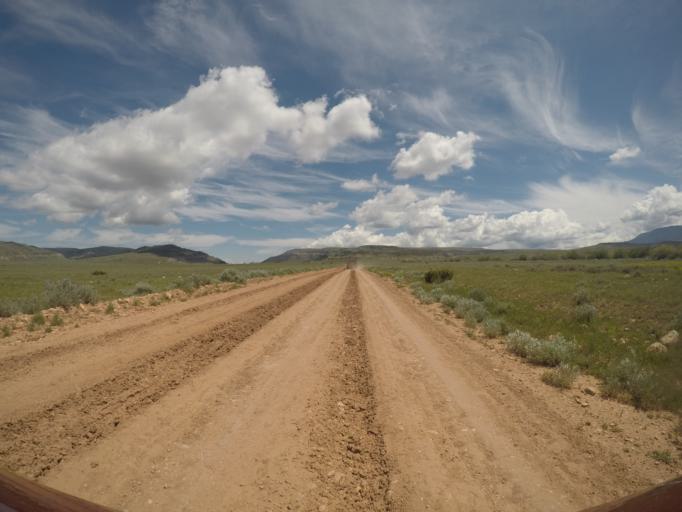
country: US
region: Montana
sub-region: Yellowstone County
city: Laurel
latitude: 45.2416
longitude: -108.6673
